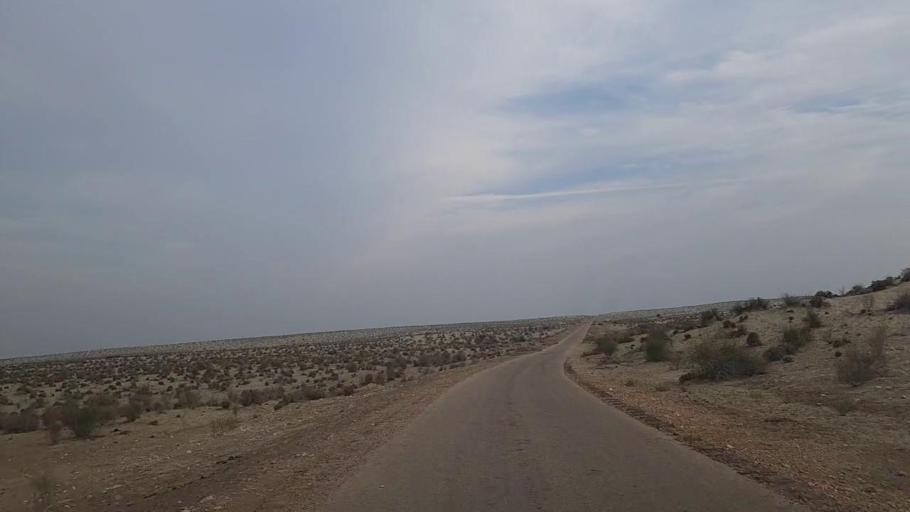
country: PK
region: Sindh
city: Daur
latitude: 26.5144
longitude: 68.5018
